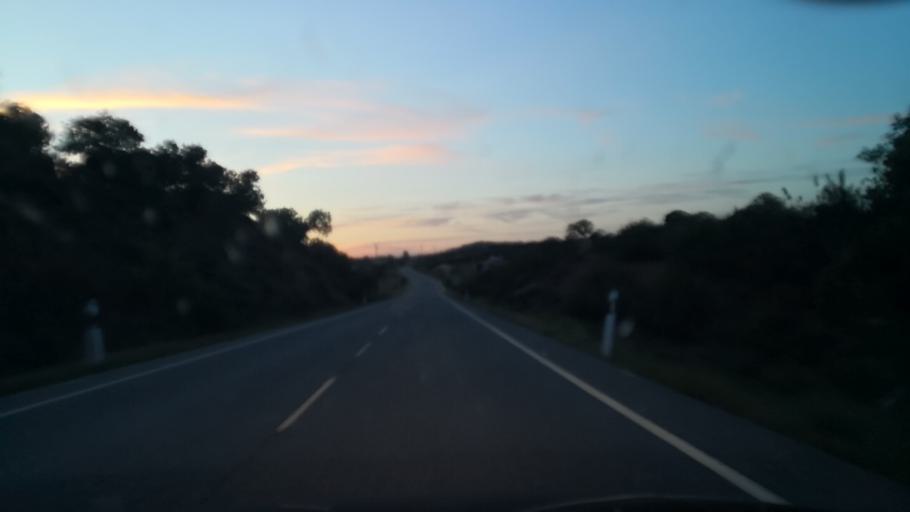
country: ES
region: Extremadura
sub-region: Provincia de Caceres
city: Piedras Albas
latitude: 39.7676
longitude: -6.9121
